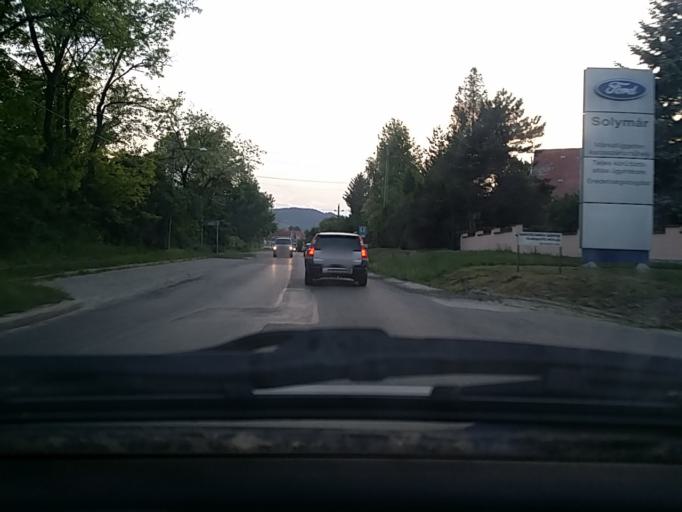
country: HU
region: Pest
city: Solymar
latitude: 47.5954
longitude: 18.9434
